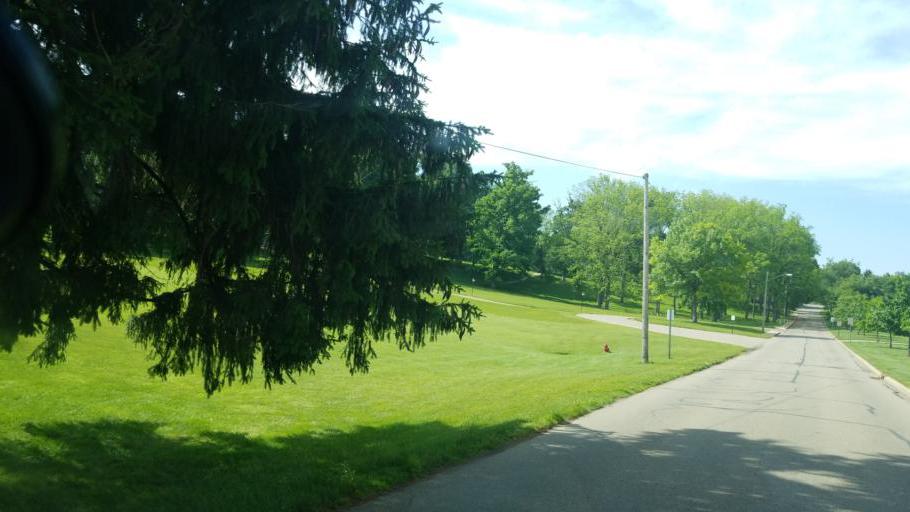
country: US
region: Ohio
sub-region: Knox County
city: Gambier
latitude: 40.3698
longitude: -82.3938
